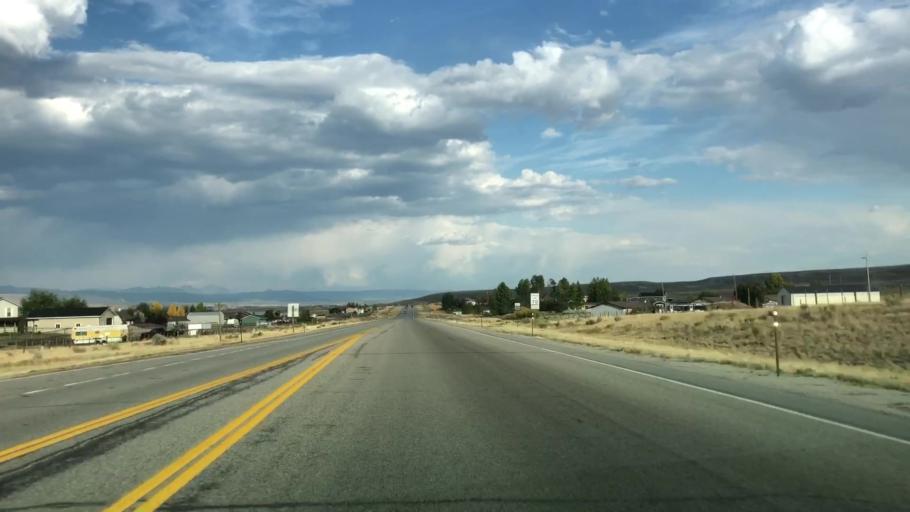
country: US
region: Wyoming
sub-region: Sublette County
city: Pinedale
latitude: 42.8804
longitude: -109.9726
